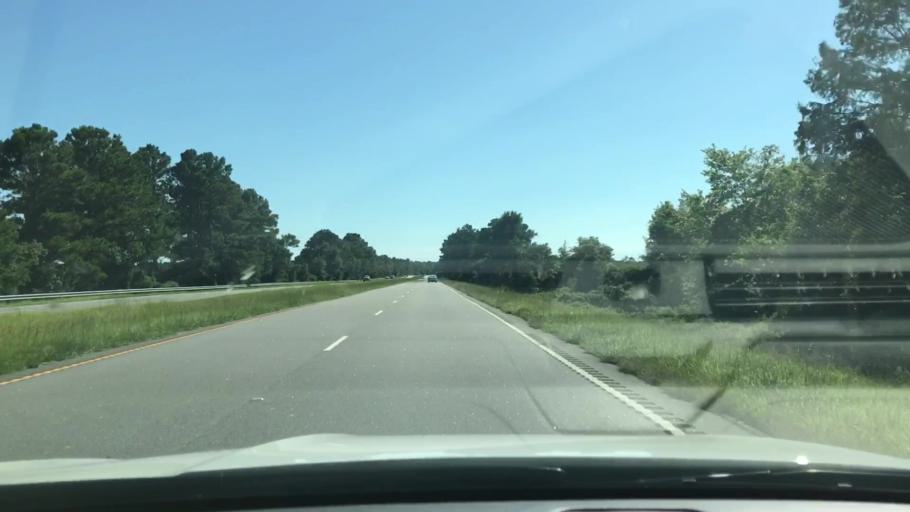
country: US
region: South Carolina
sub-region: Georgetown County
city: Georgetown
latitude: 33.1928
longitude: -79.3984
